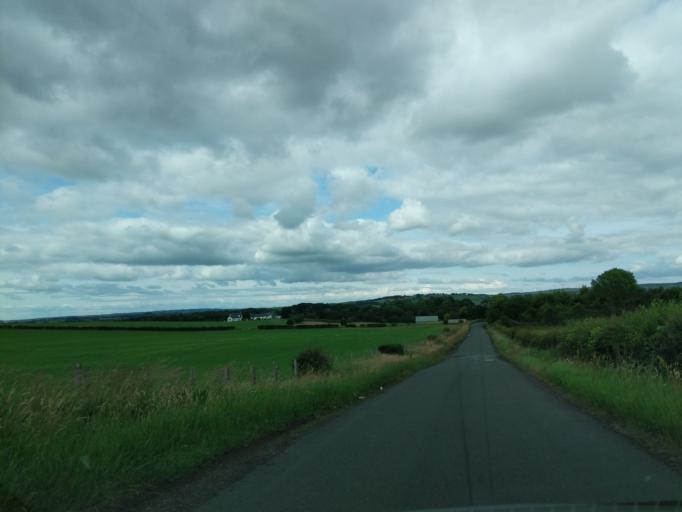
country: GB
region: Scotland
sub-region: South Lanarkshire
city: Dalserf
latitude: 55.7186
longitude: -3.9281
